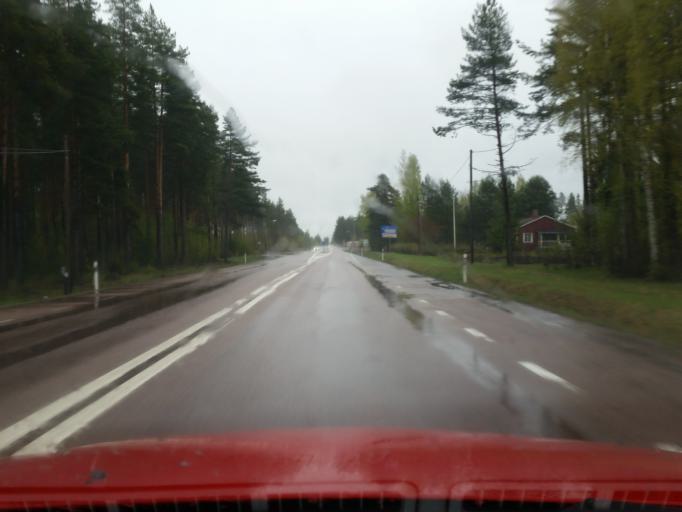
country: SE
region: Dalarna
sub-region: Borlange Kommun
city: Borlaenge
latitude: 60.5297
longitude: 15.3270
